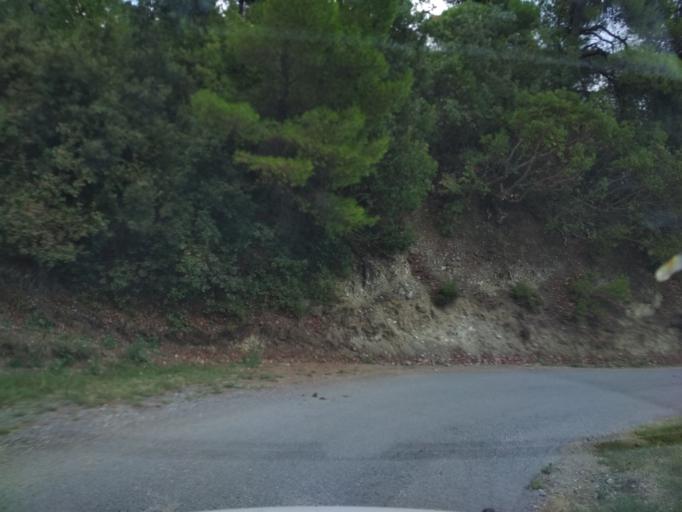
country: GR
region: Central Greece
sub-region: Nomos Evvoias
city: Roviai
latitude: 38.8499
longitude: 23.2883
